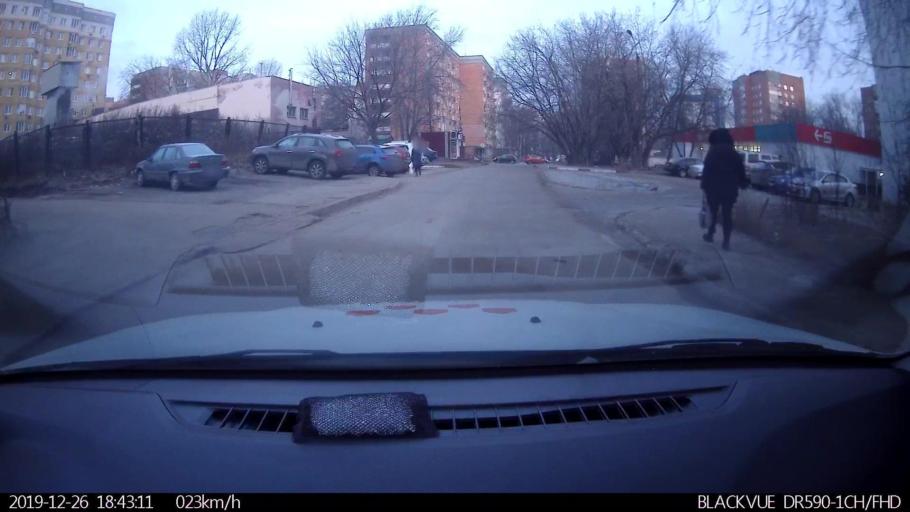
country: RU
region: Nizjnij Novgorod
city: Nizhniy Novgorod
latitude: 56.3176
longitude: 44.0302
